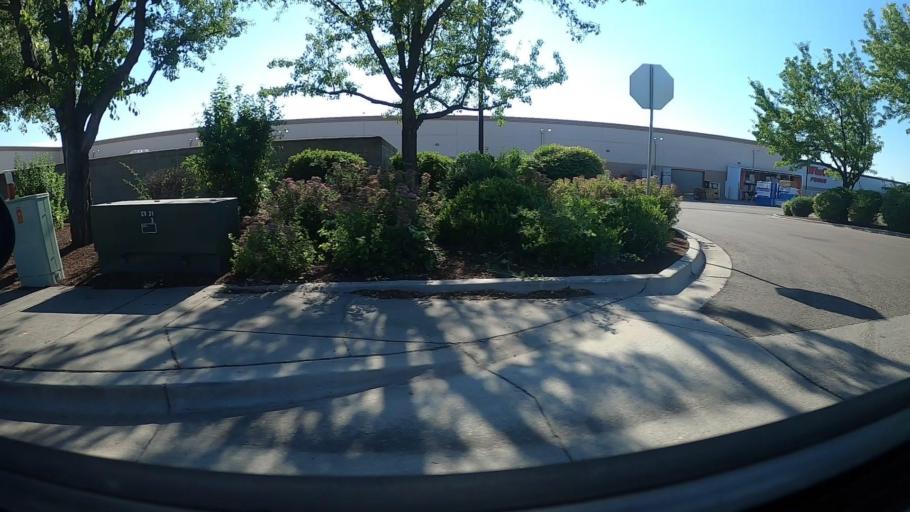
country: US
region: Idaho
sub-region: Ada County
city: Meridian
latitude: 43.5951
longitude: -116.3883
